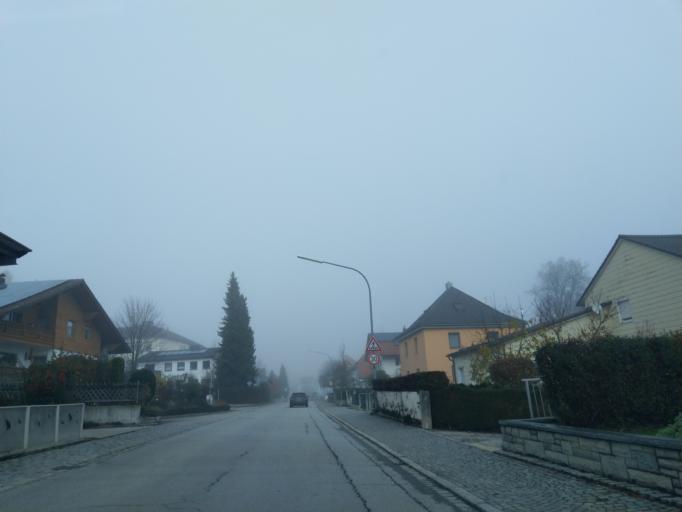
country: DE
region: Bavaria
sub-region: Lower Bavaria
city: Schollnach
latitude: 48.7520
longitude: 13.1802
